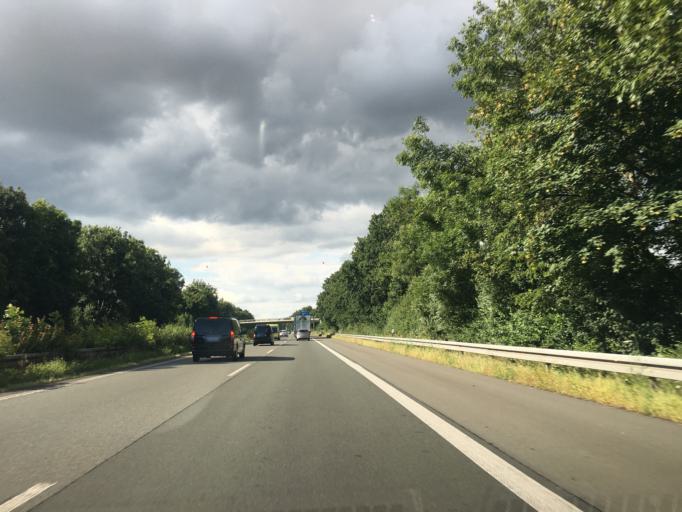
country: DE
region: North Rhine-Westphalia
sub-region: Regierungsbezirk Munster
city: Ascheberg
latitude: 51.7834
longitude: 7.6393
